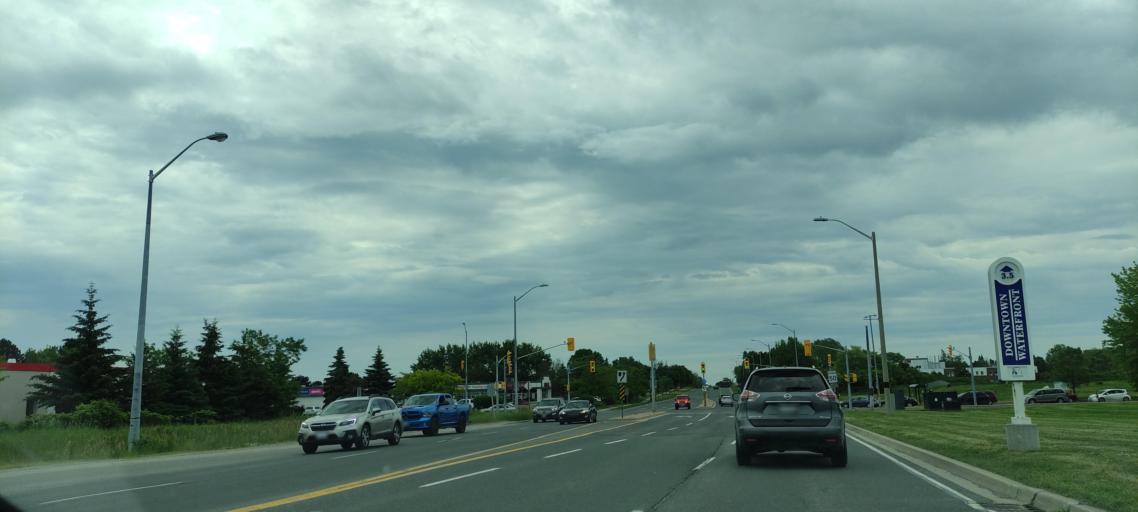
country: CA
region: Ontario
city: Cobourg
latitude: 43.9782
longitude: -78.1955
